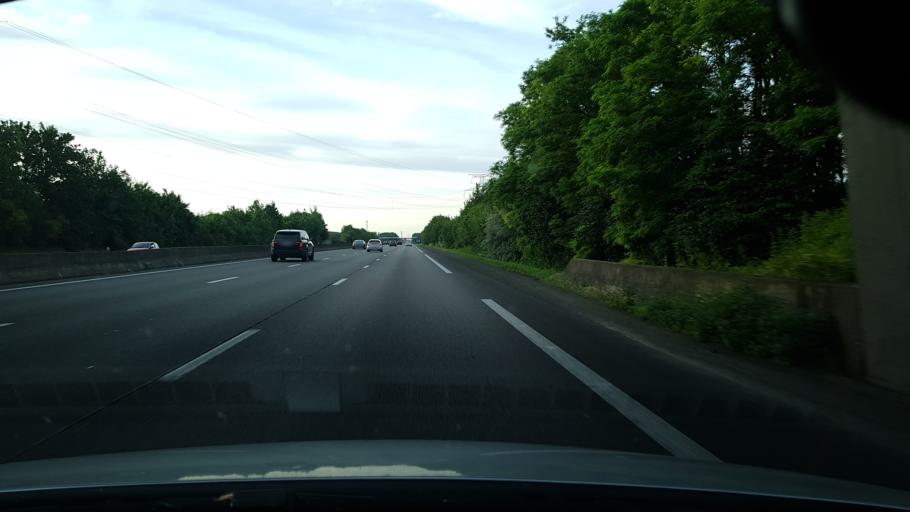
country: FR
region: Centre
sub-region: Departement du Loiret
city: Artenay
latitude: 48.0960
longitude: 1.8520
